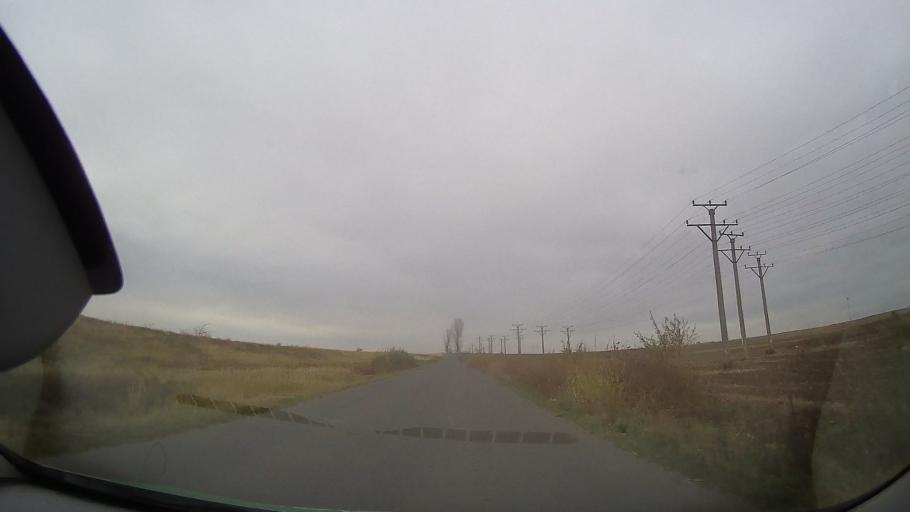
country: RO
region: Braila
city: Dudesti
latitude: 44.9040
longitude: 27.4319
